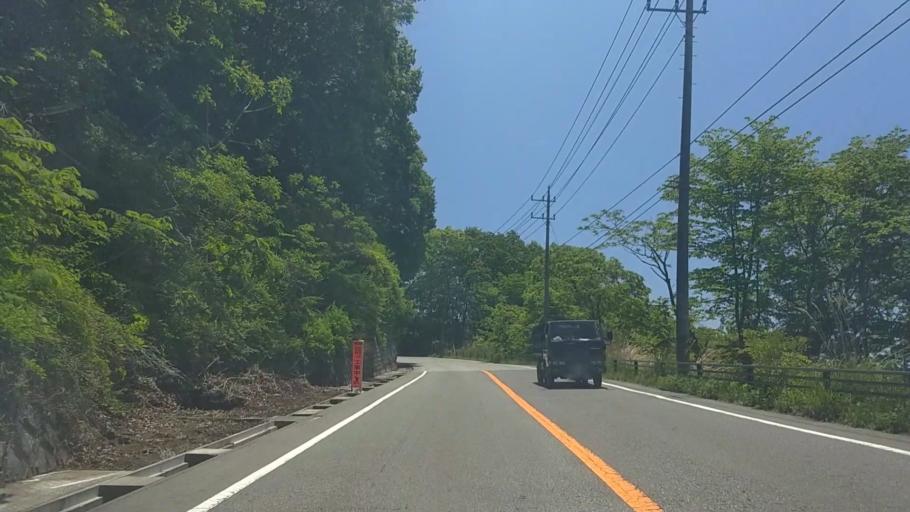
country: JP
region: Yamanashi
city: Nirasaki
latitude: 35.8796
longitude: 138.4306
